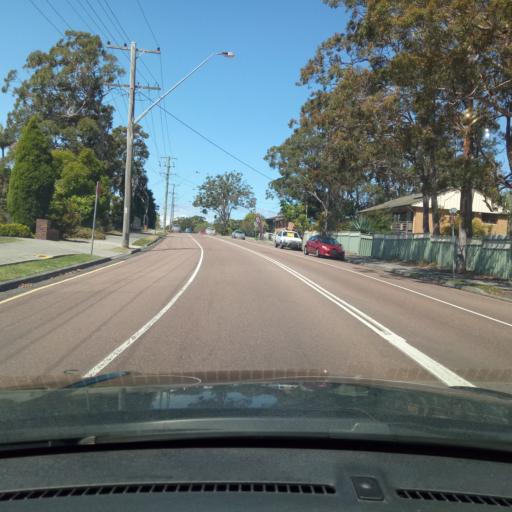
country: AU
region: New South Wales
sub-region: Wyong Shire
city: Tumbi Vmbi
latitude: -33.3714
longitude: 151.4509
